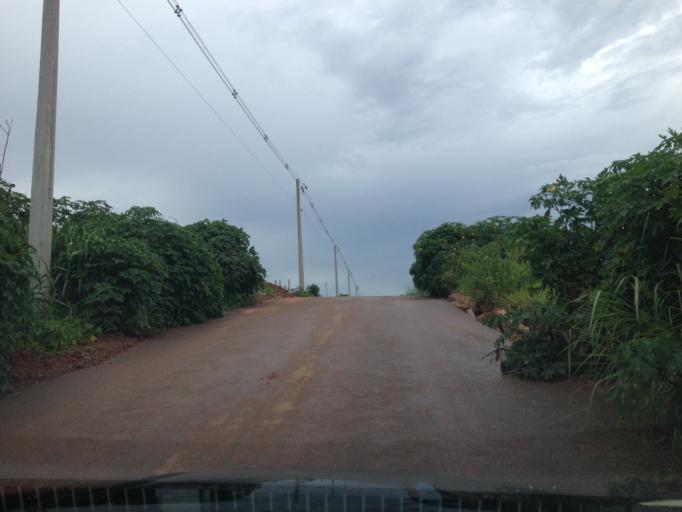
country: BR
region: Goias
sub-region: Luziania
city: Luziania
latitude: -16.0593
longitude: -47.9653
